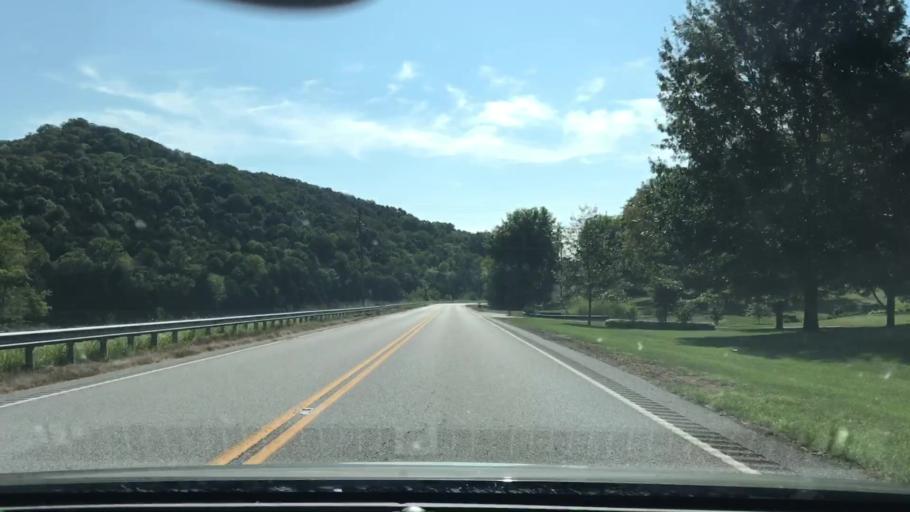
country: US
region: Tennessee
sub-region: Jackson County
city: Gainesboro
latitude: 36.3642
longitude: -85.7570
